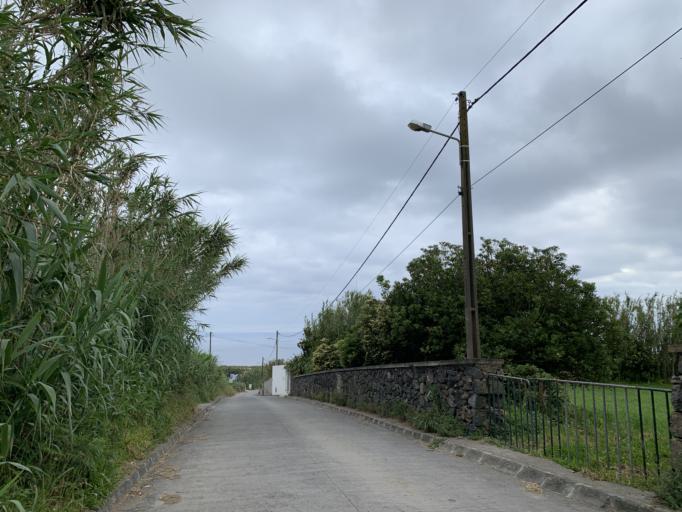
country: PT
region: Azores
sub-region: Ponta Delgada
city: Arrifes
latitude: 37.8553
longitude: -25.8470
